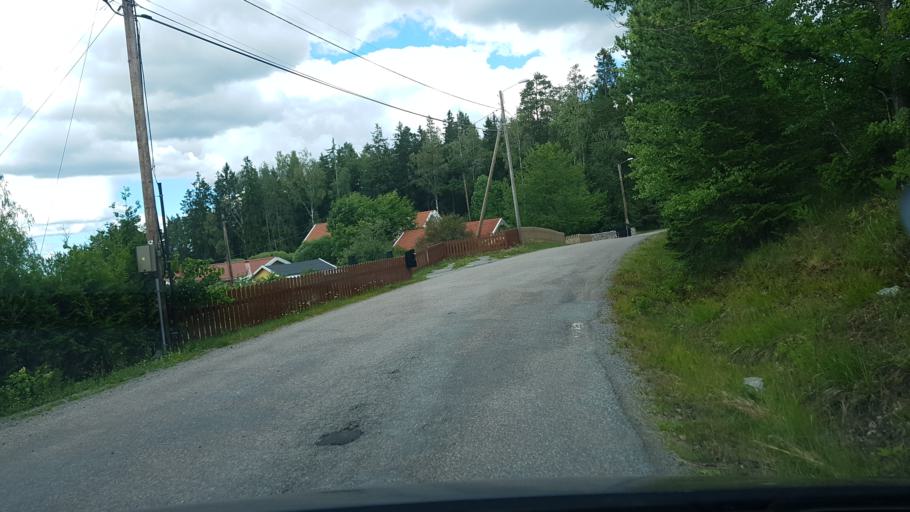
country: SE
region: Stockholm
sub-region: Upplands-Bro Kommun
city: Kungsaengen
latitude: 59.4967
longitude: 17.8056
